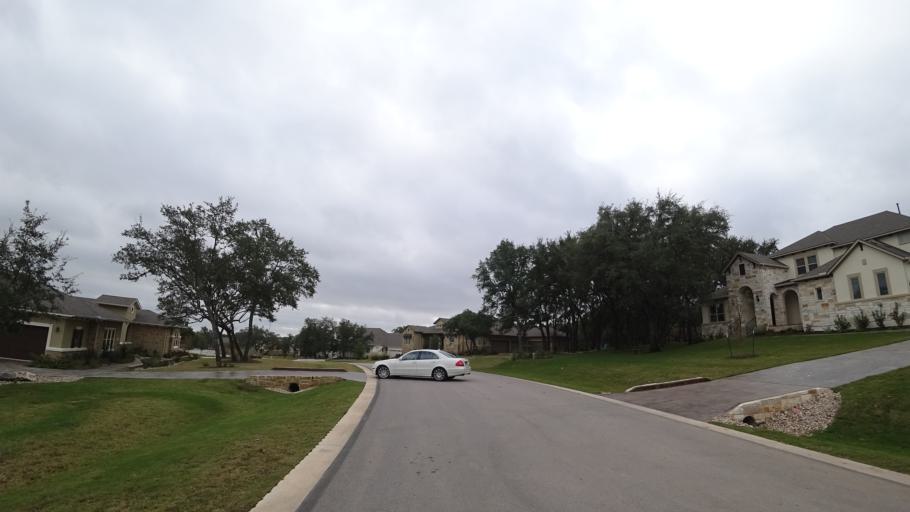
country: US
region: Texas
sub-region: Travis County
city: Barton Creek
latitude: 30.2562
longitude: -97.9134
